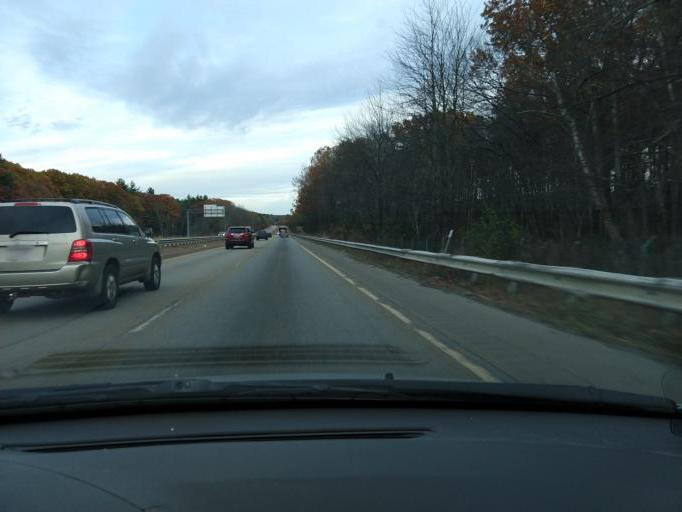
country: US
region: Massachusetts
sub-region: Middlesex County
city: Shirley
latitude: 42.5186
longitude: -71.6193
